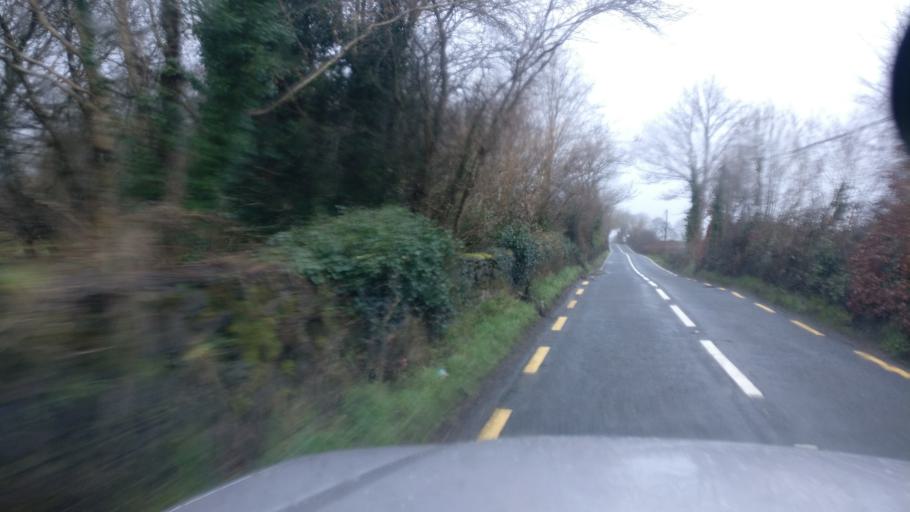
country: IE
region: Connaught
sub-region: County Galway
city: Loughrea
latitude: 53.1559
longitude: -8.4813
